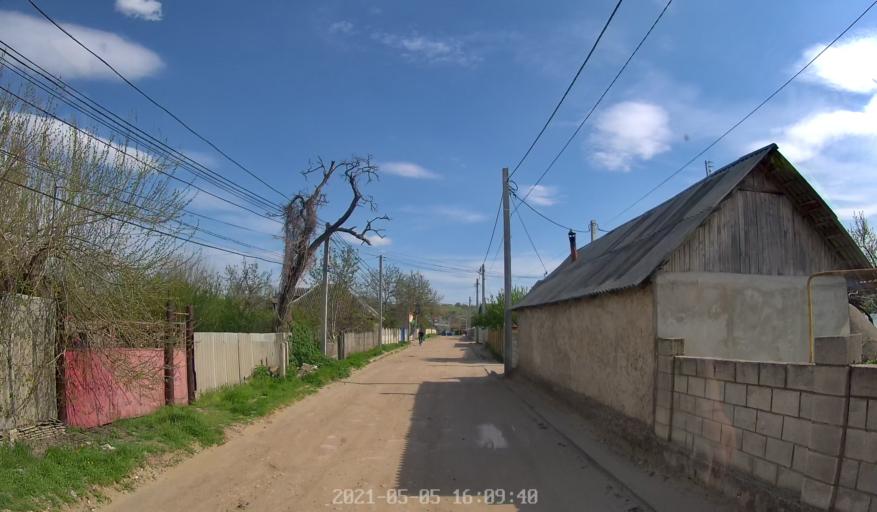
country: MD
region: Criuleni
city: Criuleni
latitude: 47.1392
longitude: 29.1994
